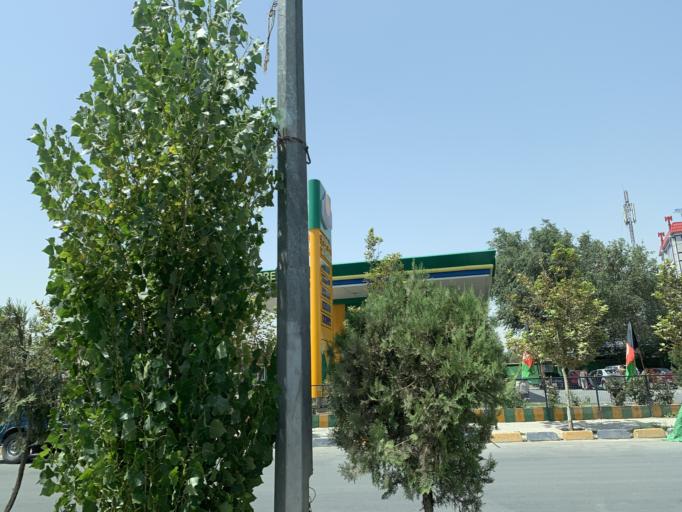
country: AF
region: Kabul
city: Kabul
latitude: 34.5005
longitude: 69.1568
